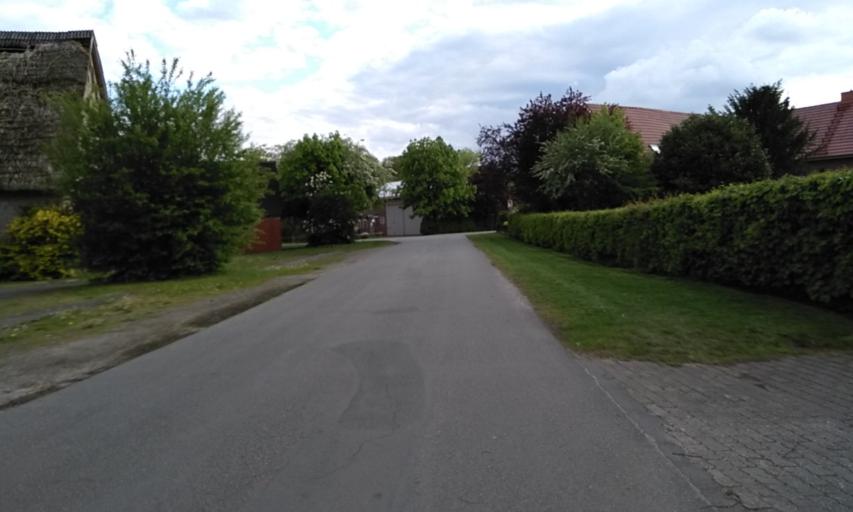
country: DE
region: Lower Saxony
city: Wohnste
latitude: 53.3857
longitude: 9.5538
